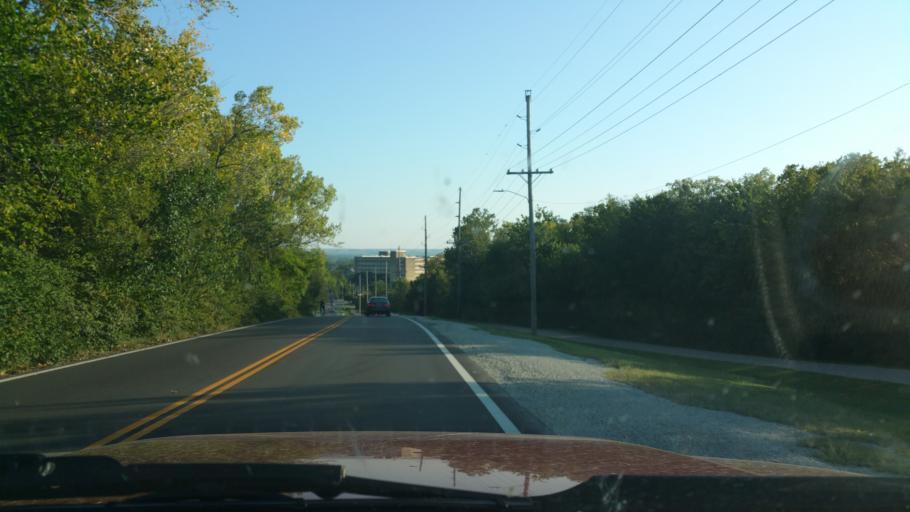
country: US
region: Kansas
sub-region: Riley County
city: Manhattan
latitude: 39.1998
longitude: -96.5763
